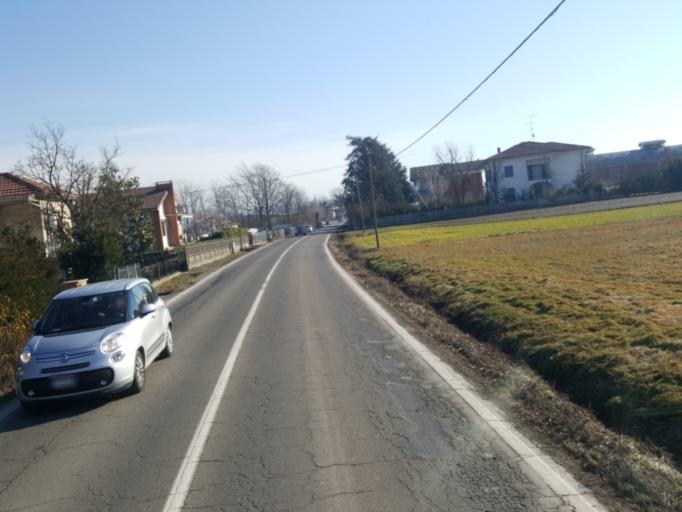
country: IT
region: Piedmont
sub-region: Provincia di Alessandria
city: Viguzzolo
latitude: 44.9060
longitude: 8.9333
